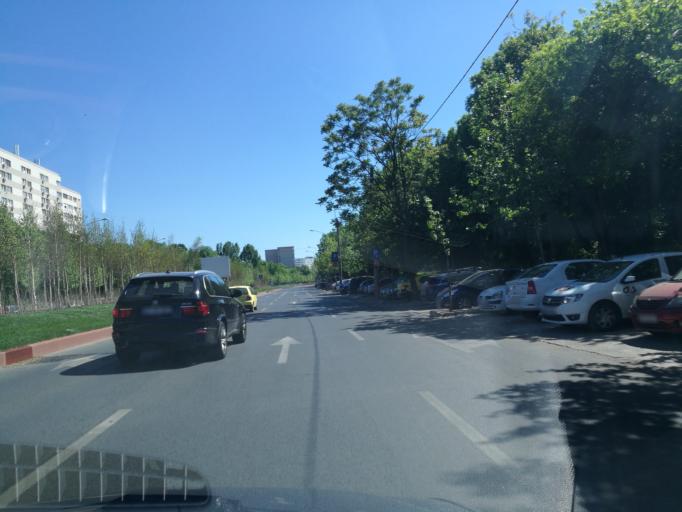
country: RO
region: Ilfov
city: Dobroesti
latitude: 44.4203
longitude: 26.1644
